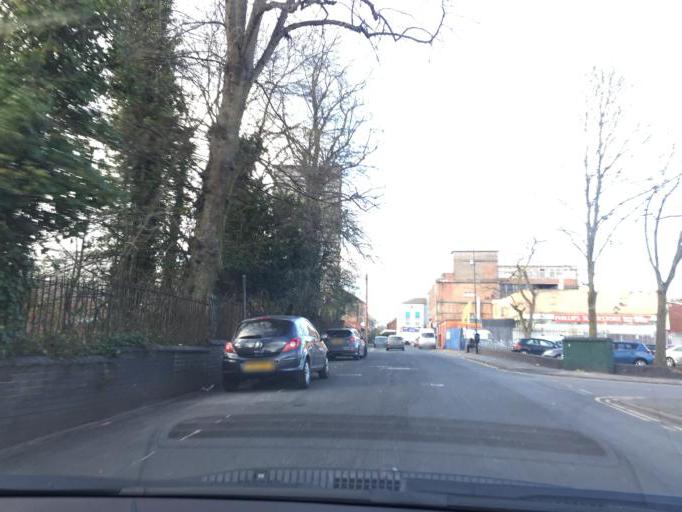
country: GB
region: England
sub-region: Coventry
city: Coventry
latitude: 52.4124
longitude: -1.4998
